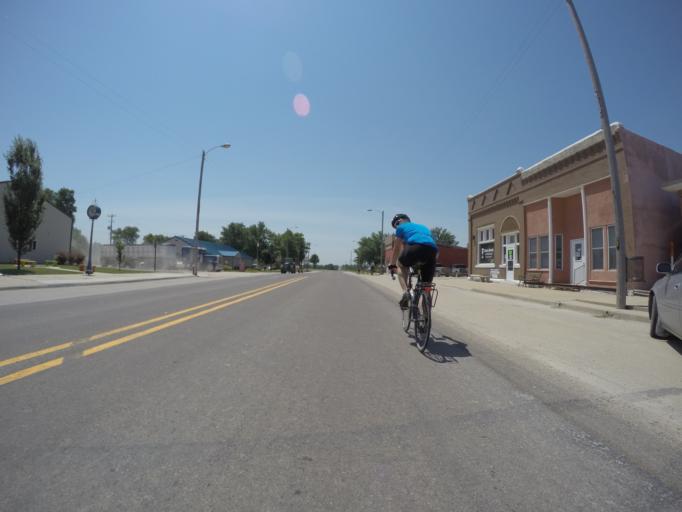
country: US
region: Nebraska
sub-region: Pawnee County
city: Pawnee City
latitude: 40.0341
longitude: -96.0482
